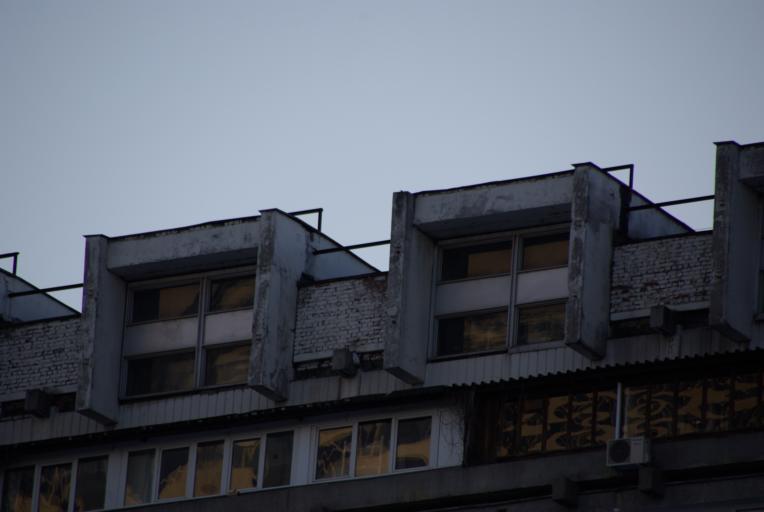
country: RU
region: Moscow
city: Kotlovka
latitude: 55.6388
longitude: 37.5970
